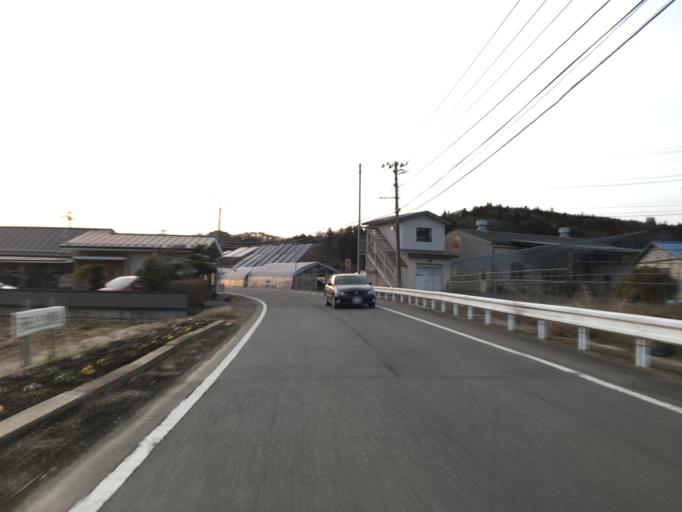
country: JP
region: Fukushima
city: Ishikawa
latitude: 37.0661
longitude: 140.3388
